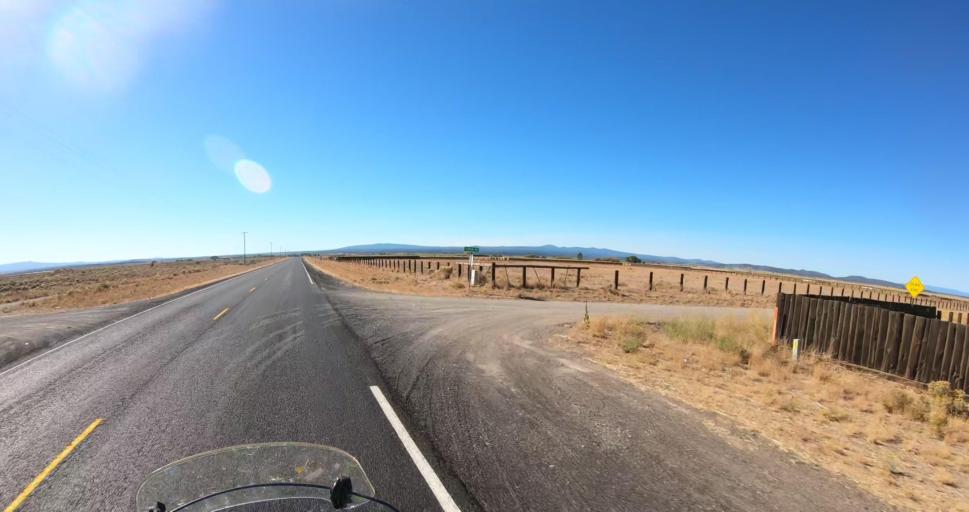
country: US
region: Oregon
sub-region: Deschutes County
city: La Pine
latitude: 43.1276
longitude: -121.0065
